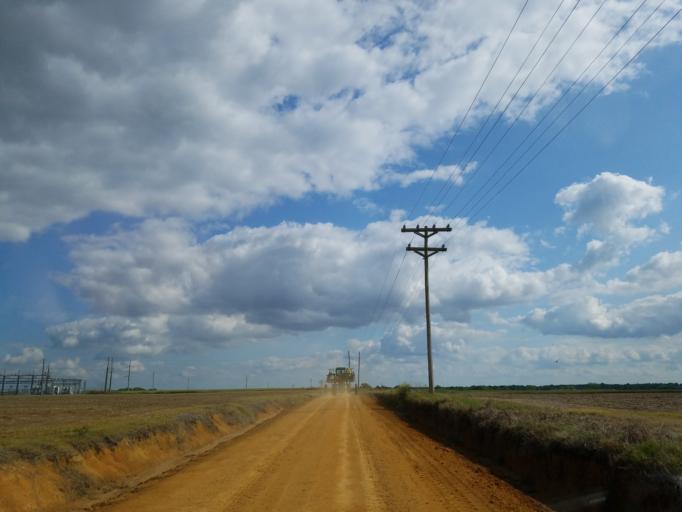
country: US
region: Georgia
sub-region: Dooly County
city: Vienna
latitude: 32.1461
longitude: -83.7859
